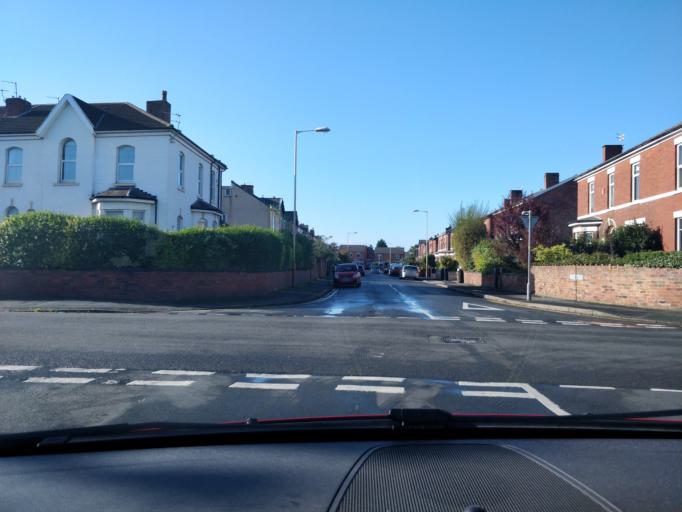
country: GB
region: England
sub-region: Sefton
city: Southport
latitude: 53.6371
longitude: -3.0030
